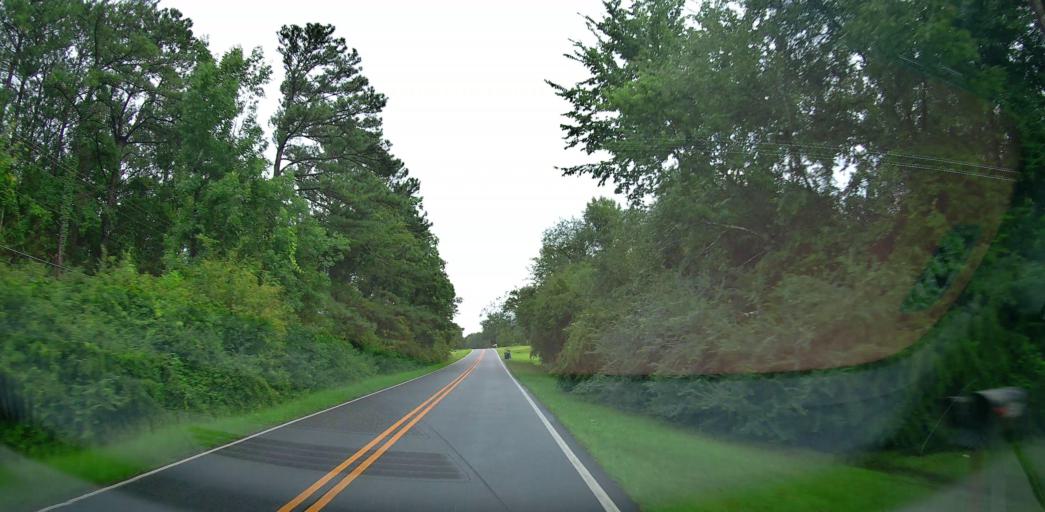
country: US
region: Georgia
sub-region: Peach County
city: Byron
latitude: 32.7434
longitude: -83.7051
